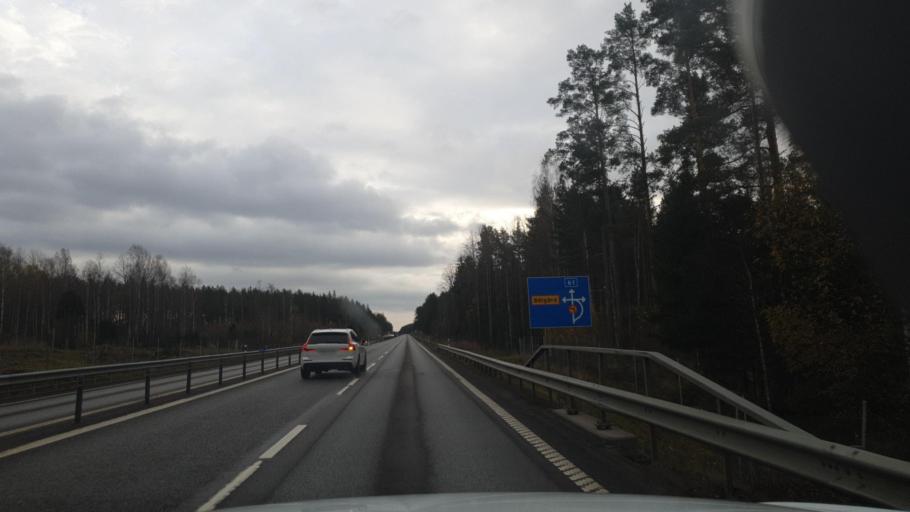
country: SE
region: Vaermland
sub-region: Arvika Kommun
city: Arvika
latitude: 59.6511
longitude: 12.6744
